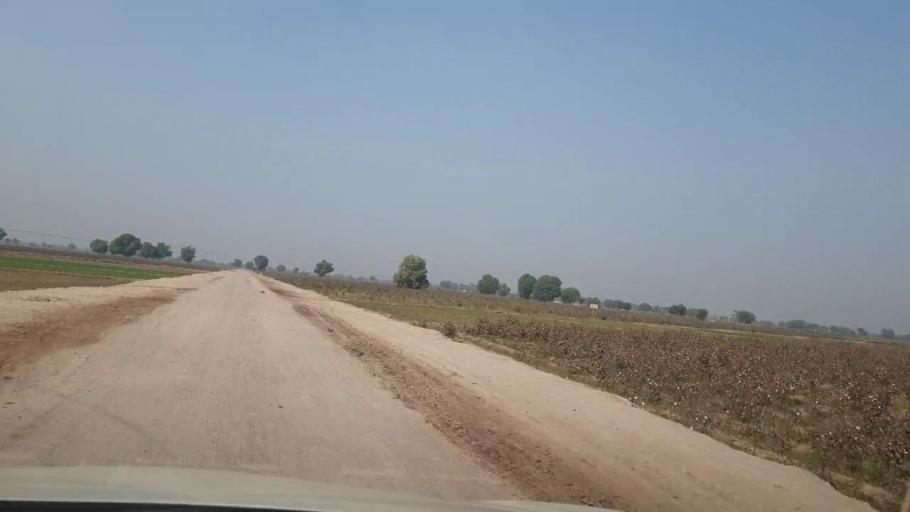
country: PK
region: Sindh
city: Bhan
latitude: 26.5284
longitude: 67.7562
